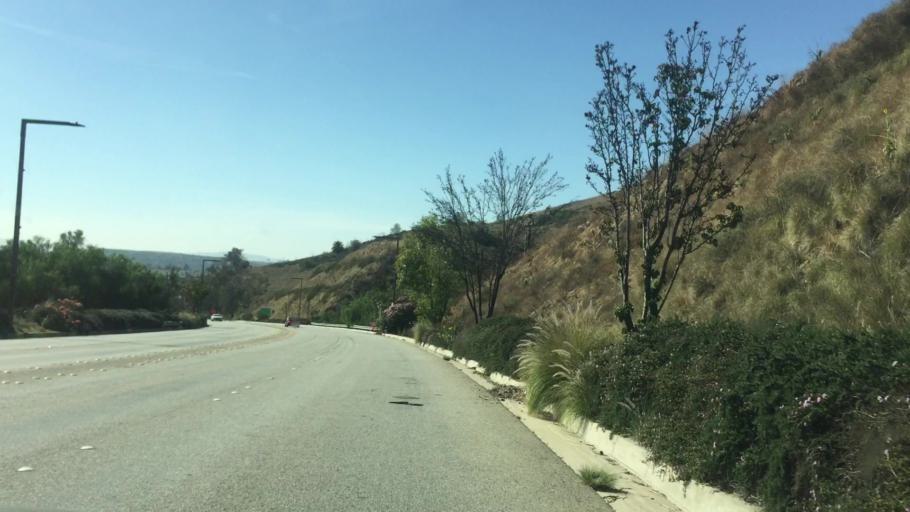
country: US
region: California
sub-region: Los Angeles County
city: La Verne
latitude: 34.0761
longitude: -117.7843
